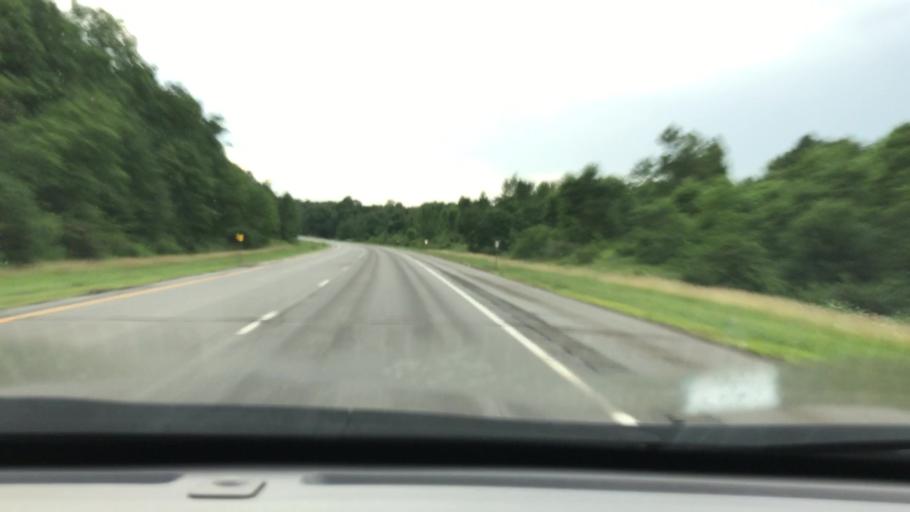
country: US
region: New York
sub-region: Erie County
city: Springville
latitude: 42.5717
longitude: -78.7147
